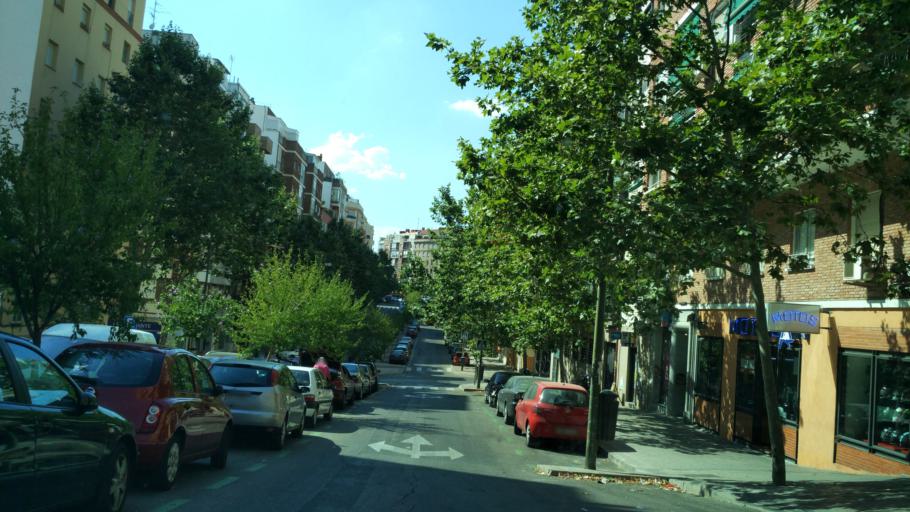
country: ES
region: Madrid
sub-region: Provincia de Madrid
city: Tetuan de las Victorias
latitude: 40.4548
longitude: -3.7057
